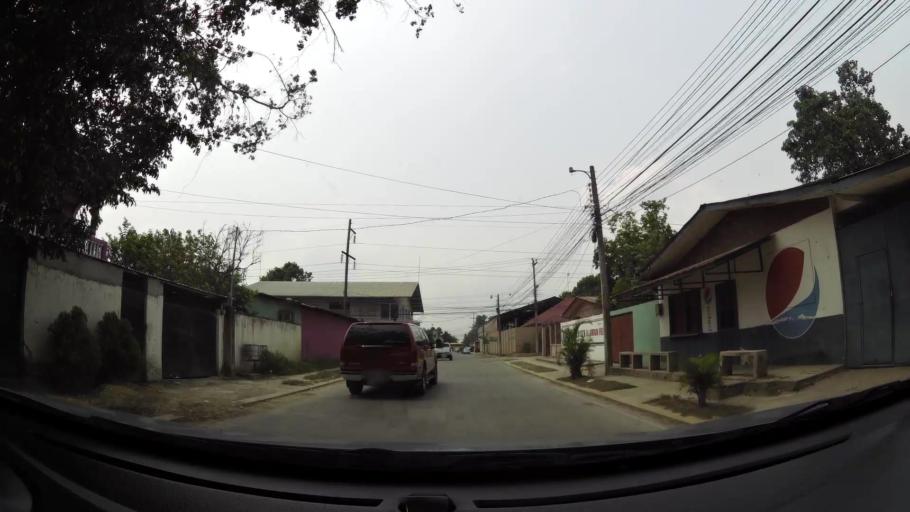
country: HN
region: Yoro
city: El Progreso
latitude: 15.4044
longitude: -87.8053
